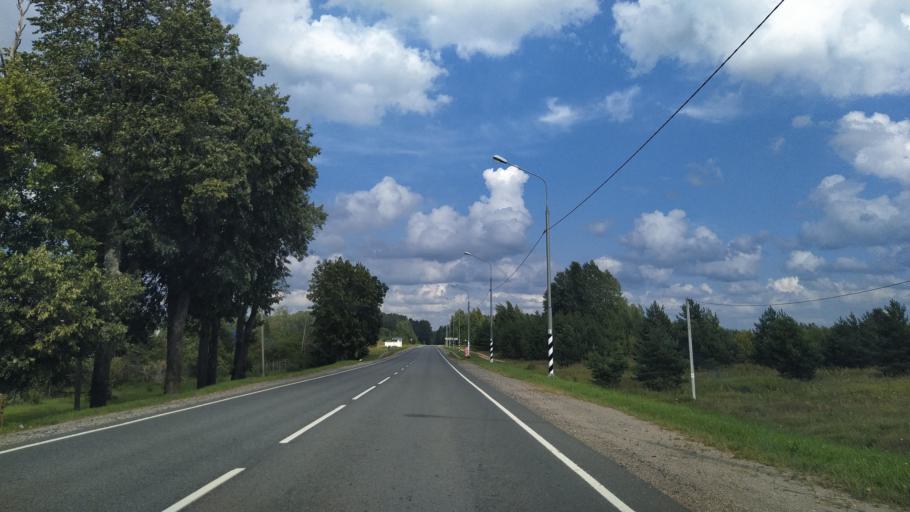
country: RU
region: Novgorod
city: Sol'tsy
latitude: 58.1022
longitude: 30.2035
